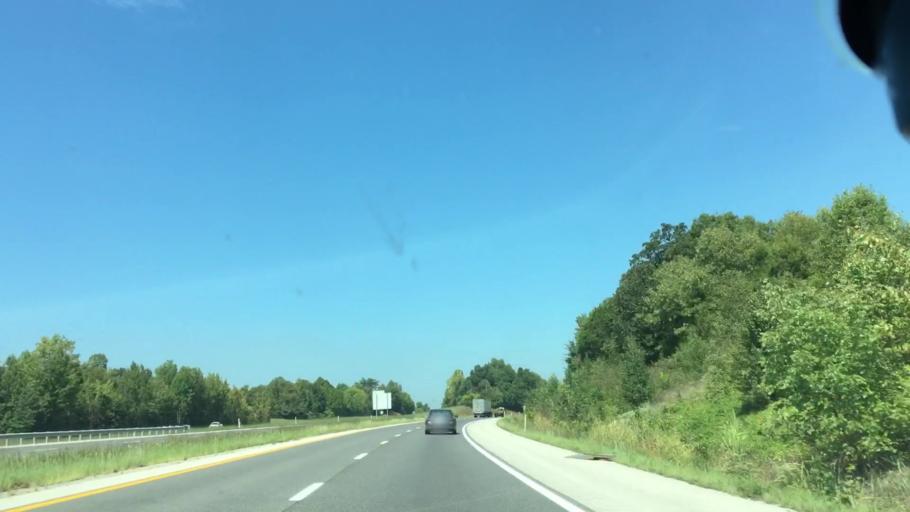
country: US
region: Kentucky
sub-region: Hopkins County
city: Madisonville
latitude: 37.3599
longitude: -87.4903
